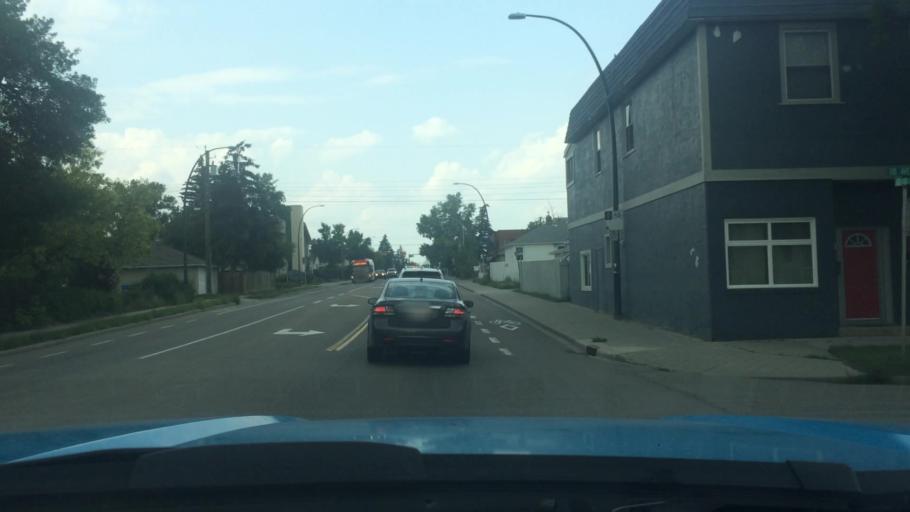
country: CA
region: Alberta
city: Calgary
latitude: 51.0687
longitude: -114.0848
